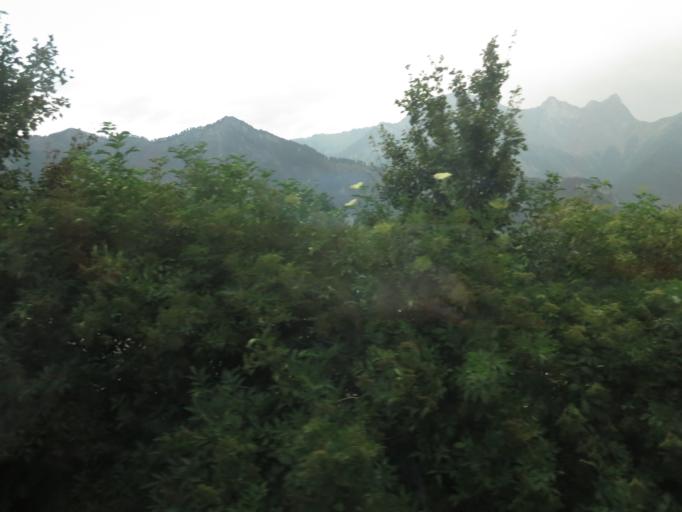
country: CH
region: Saint Gallen
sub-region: Wahlkreis Sarganserland
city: Bad Ragaz
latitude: 47.0182
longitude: 9.4902
